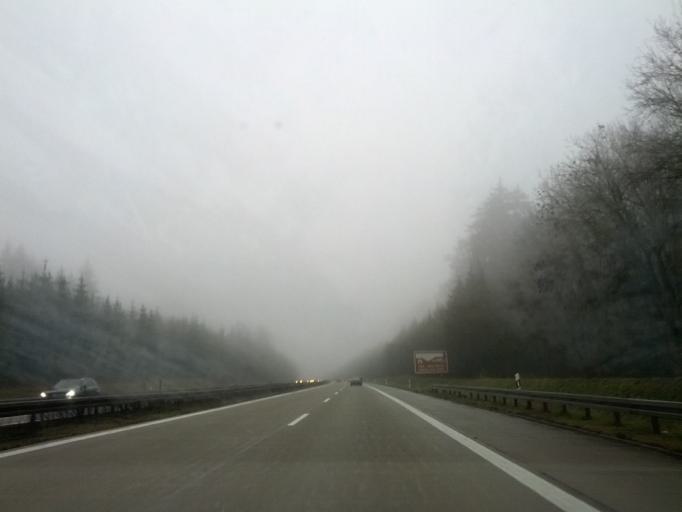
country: DE
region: Baden-Wuerttemberg
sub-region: Regierungsbezirk Stuttgart
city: Nattheim
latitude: 48.7632
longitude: 10.2065
